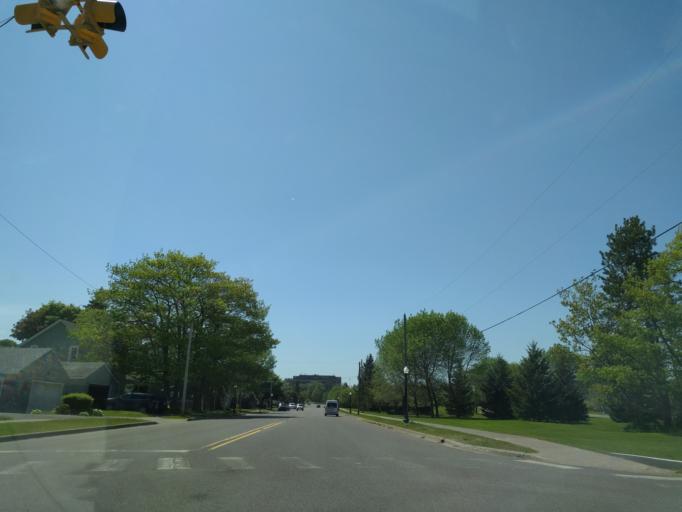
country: US
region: Michigan
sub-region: Marquette County
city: Marquette
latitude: 46.5565
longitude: -87.3893
